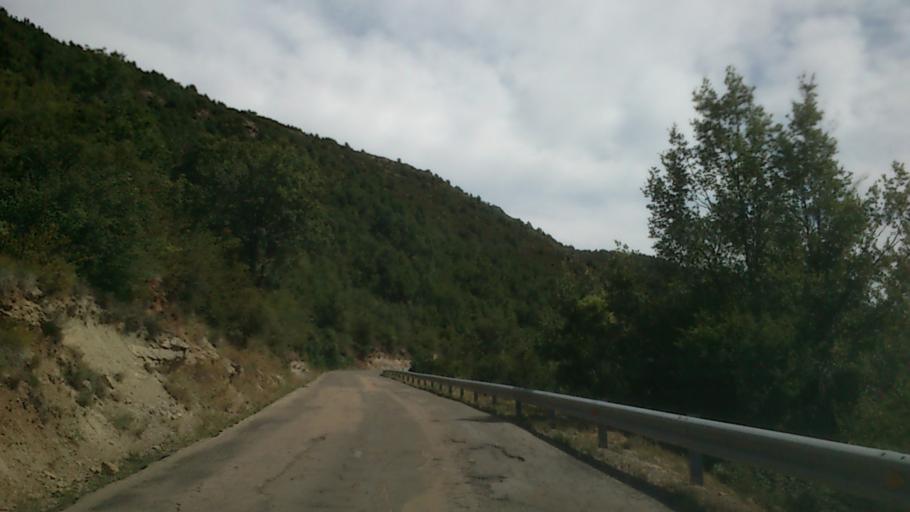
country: ES
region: Aragon
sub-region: Provincia de Huesca
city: Arguis
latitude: 42.3229
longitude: -0.4306
